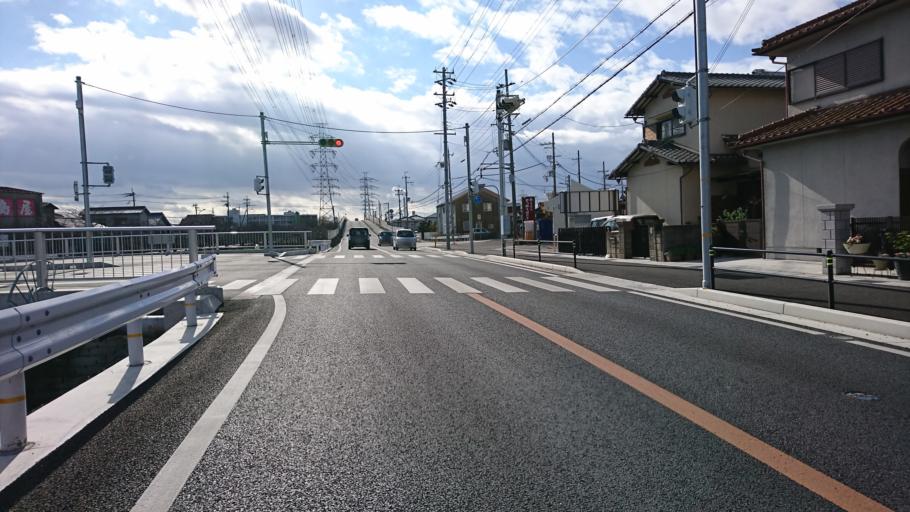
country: JP
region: Hyogo
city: Kakogawacho-honmachi
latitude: 34.7763
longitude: 134.7787
